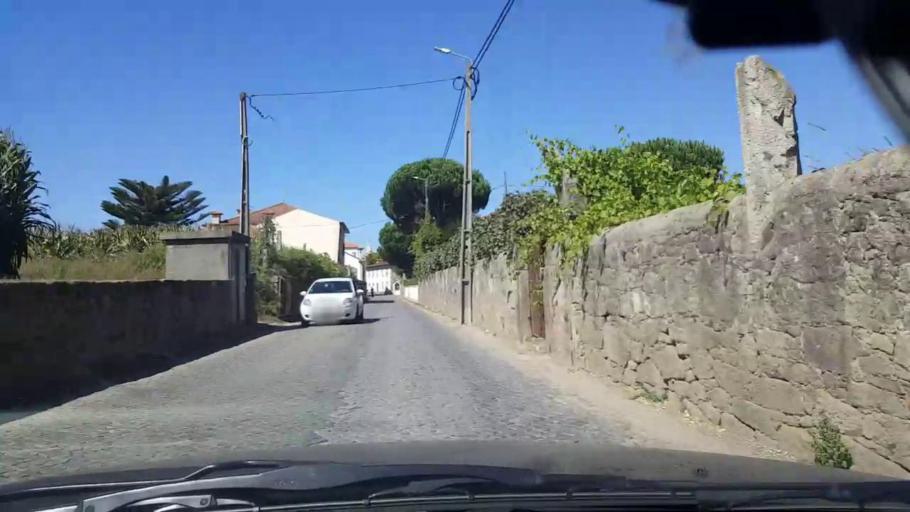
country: PT
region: Porto
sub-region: Vila do Conde
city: Arvore
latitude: 41.3226
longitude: -8.7022
